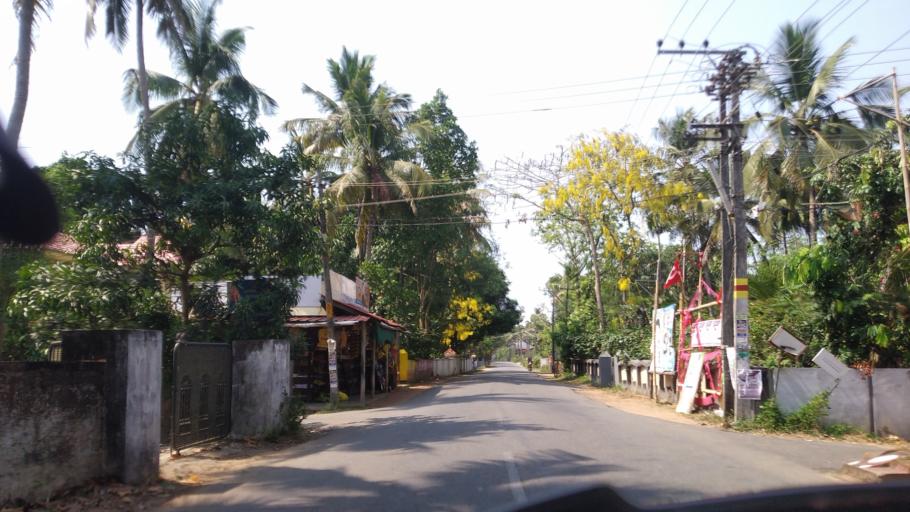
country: IN
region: Kerala
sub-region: Thrissur District
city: Kodungallur
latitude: 10.2576
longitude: 76.1458
